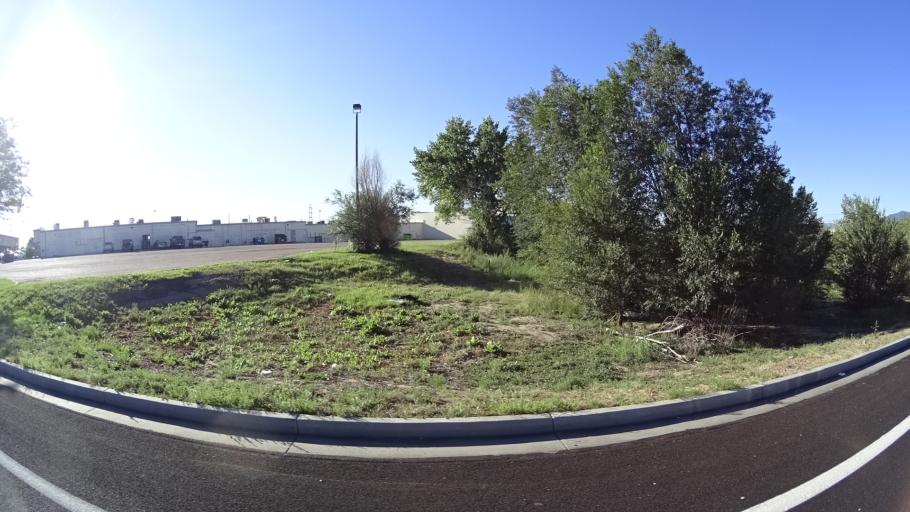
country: US
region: Colorado
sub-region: El Paso County
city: Stratmoor
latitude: 38.7917
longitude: -104.7612
